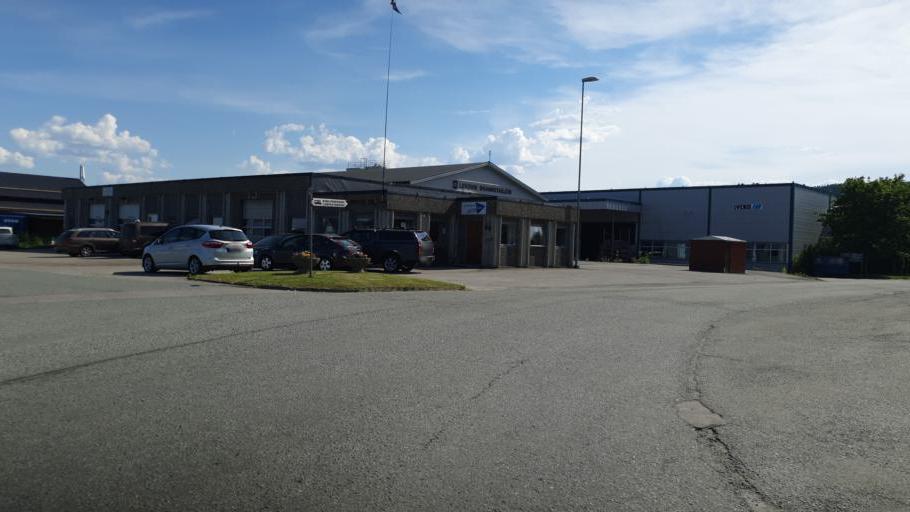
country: NO
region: Nord-Trondelag
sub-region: Leksvik
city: Leksvik
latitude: 63.6687
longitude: 10.6168
